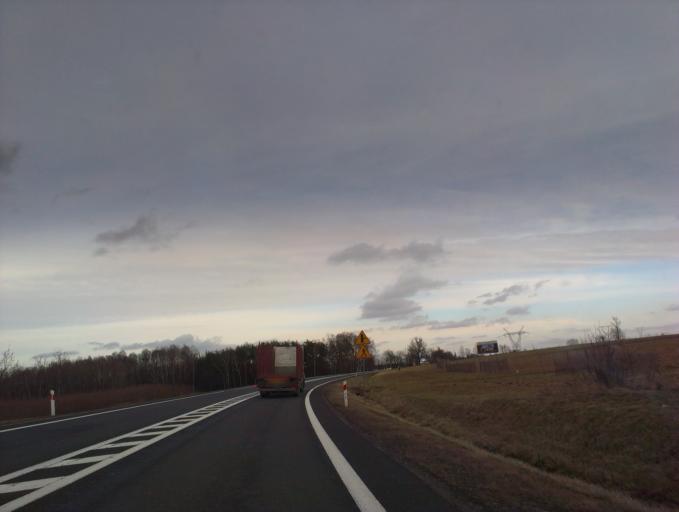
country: PL
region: Masovian Voivodeship
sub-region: Powiat sierpecki
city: Szczutowo
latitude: 52.9043
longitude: 19.4920
